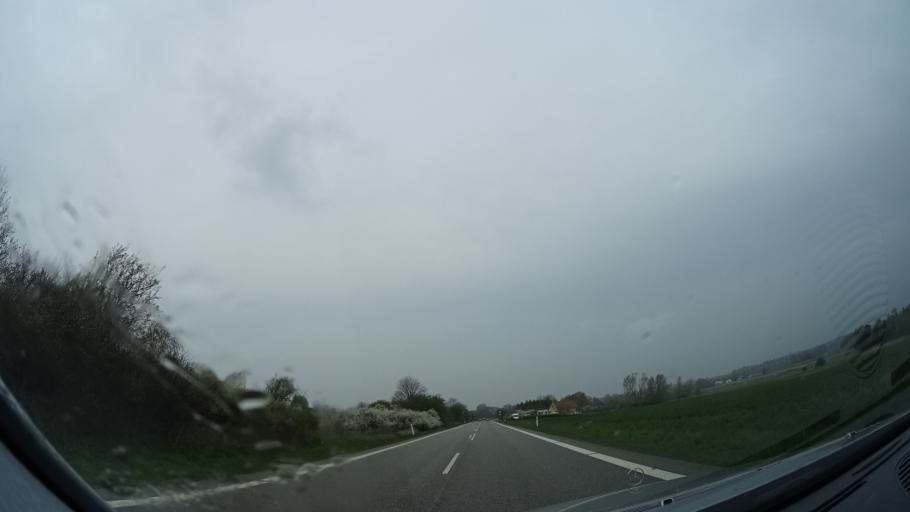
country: DK
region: Zealand
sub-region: Holbaek Kommune
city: Holbaek
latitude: 55.7193
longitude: 11.6433
